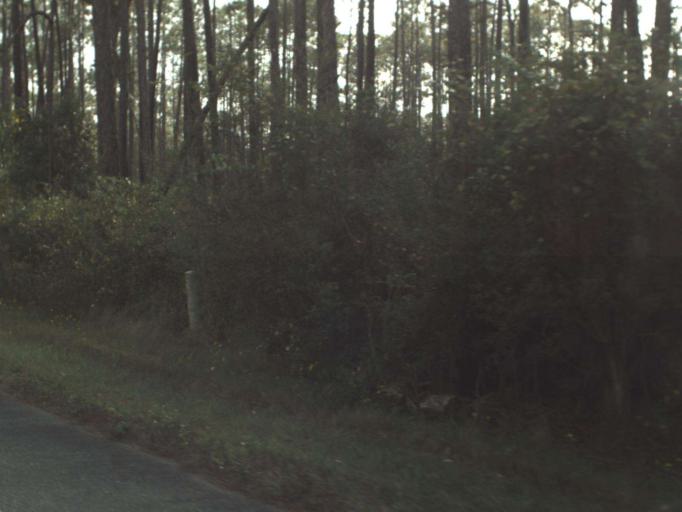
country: US
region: Florida
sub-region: Franklin County
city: Apalachicola
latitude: 29.9573
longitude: -84.9762
